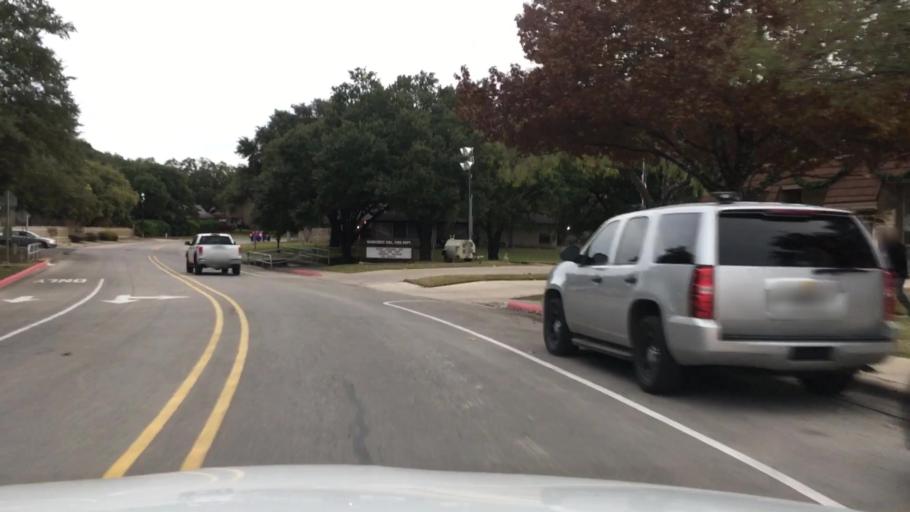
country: US
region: Texas
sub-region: Bexar County
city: Windcrest
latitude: 29.5170
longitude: -98.3814
